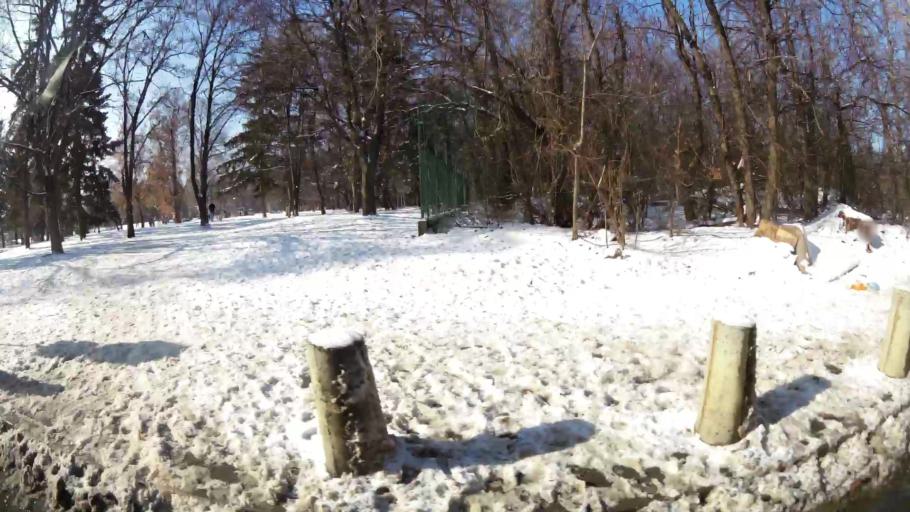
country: BG
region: Sofia-Capital
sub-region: Stolichna Obshtina
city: Sofia
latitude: 42.6613
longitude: 23.3134
